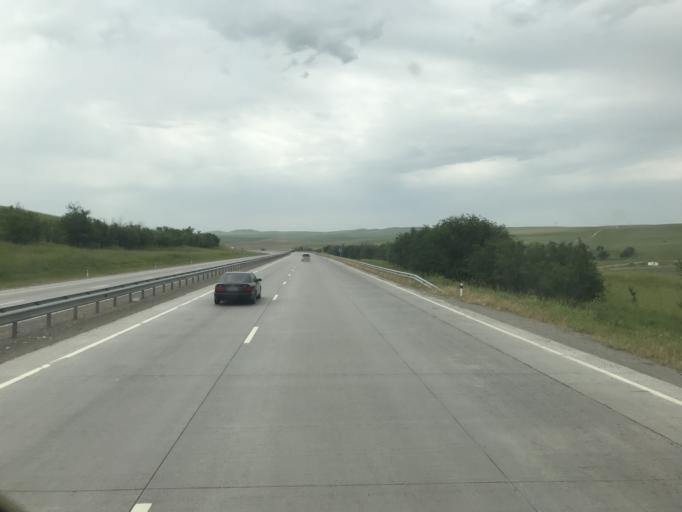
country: KZ
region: Ongtustik Qazaqstan
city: Shymkent
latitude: 42.1774
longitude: 69.4942
